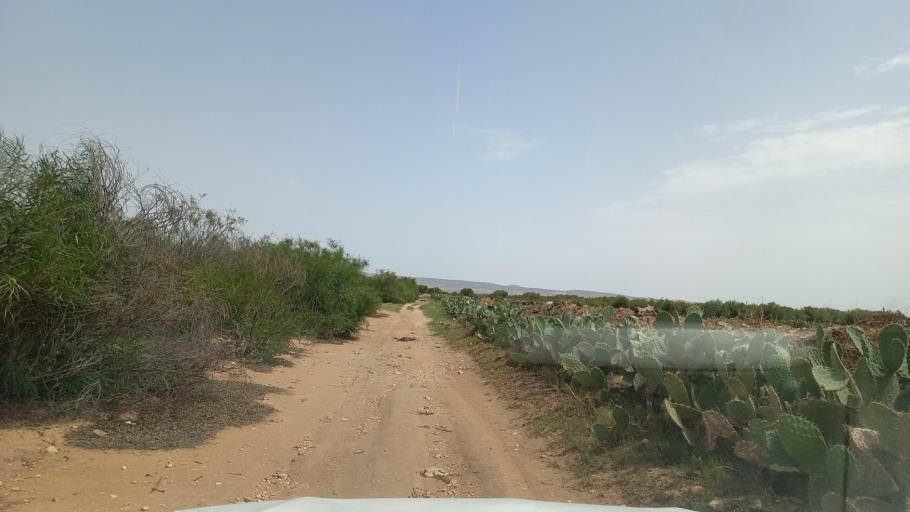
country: TN
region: Al Qasrayn
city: Kasserine
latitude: 35.2929
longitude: 9.0161
